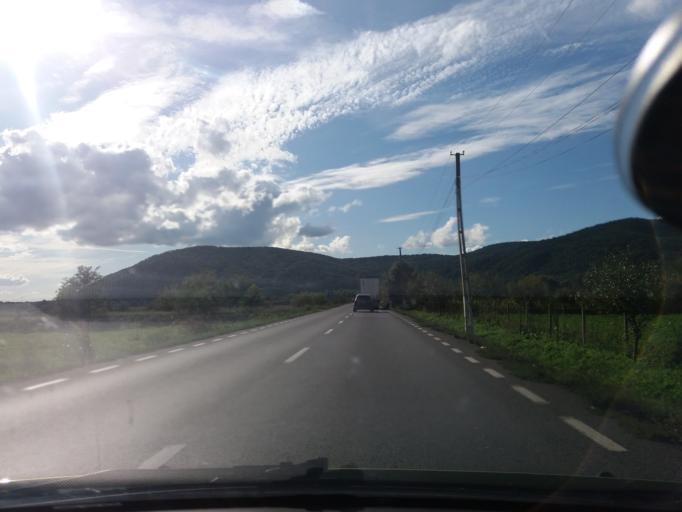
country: RO
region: Arad
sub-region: Comuna Barzava
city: Barzava
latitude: 46.1115
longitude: 21.9692
